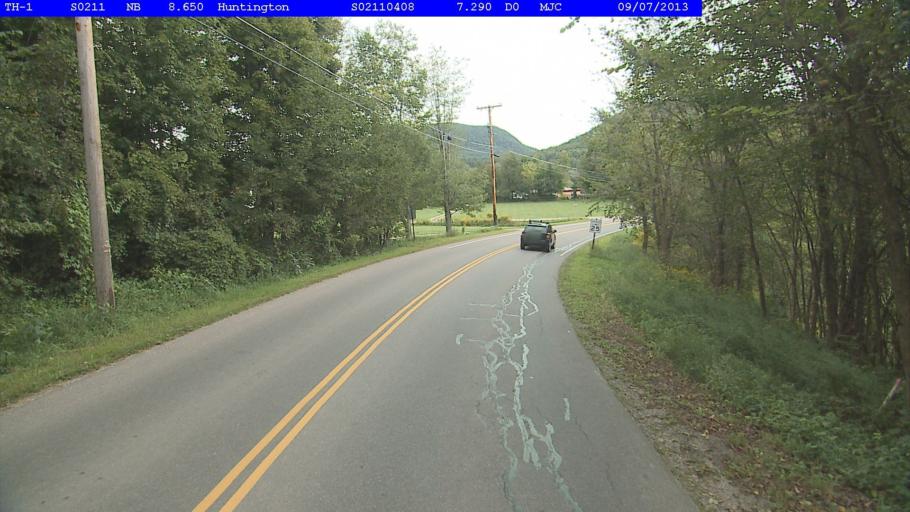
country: US
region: Vermont
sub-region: Chittenden County
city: Hinesburg
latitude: 44.3237
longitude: -72.9884
